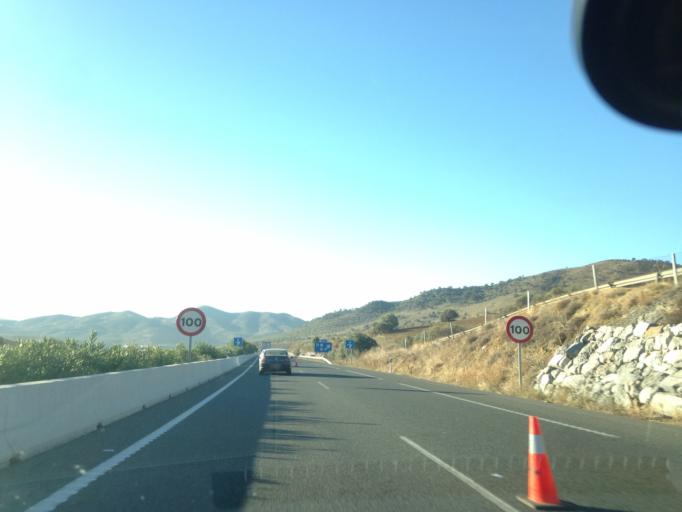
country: ES
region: Andalusia
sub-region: Provincia de Malaga
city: Casabermeja
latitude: 36.9315
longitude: -4.4461
